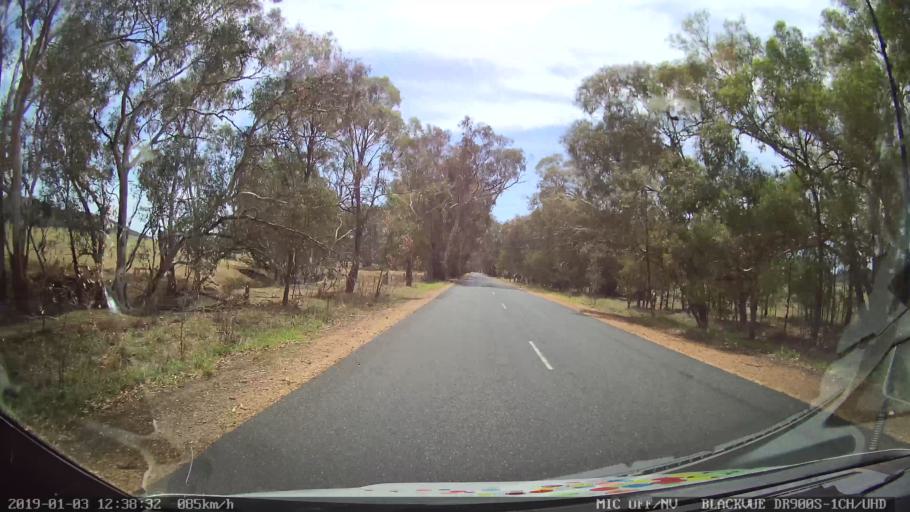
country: AU
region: New South Wales
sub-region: Weddin
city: Grenfell
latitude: -33.8327
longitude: 148.1967
